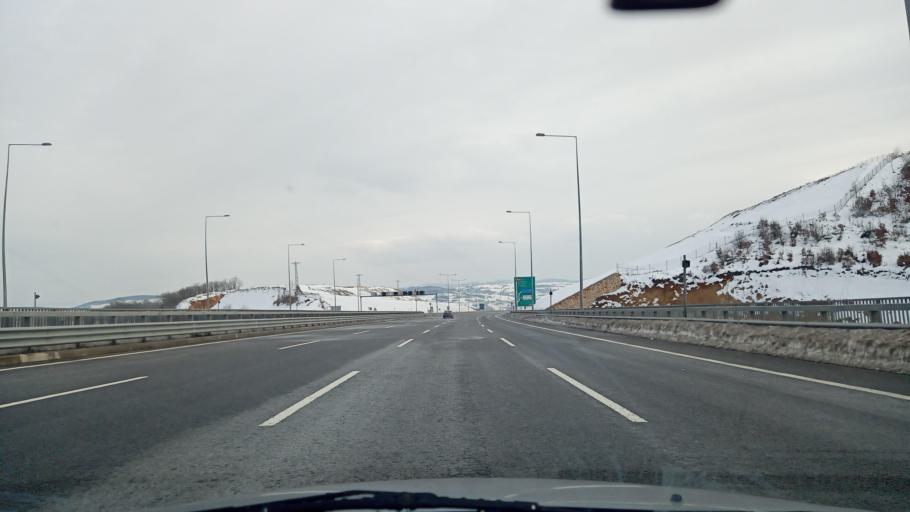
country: TR
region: Kocaeli
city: Korfez
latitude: 40.8883
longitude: 29.7357
